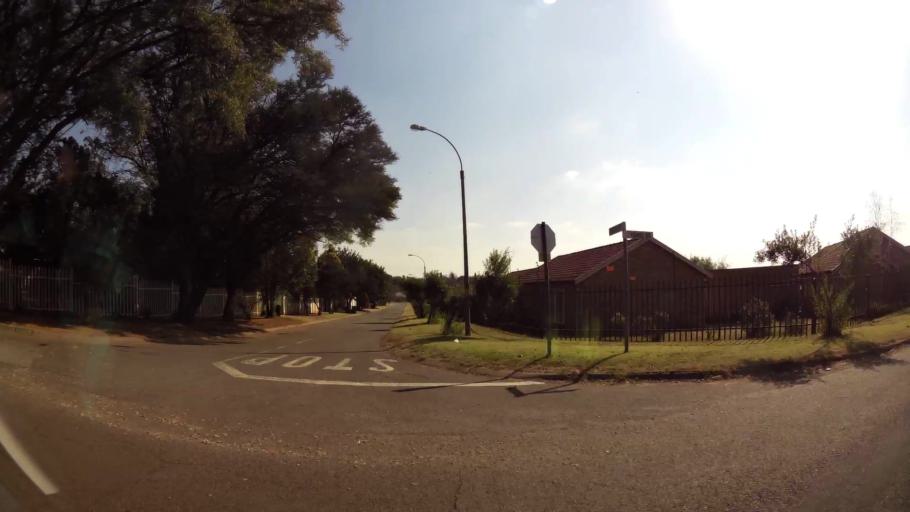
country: ZA
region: Gauteng
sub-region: City of Johannesburg Metropolitan Municipality
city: Modderfontein
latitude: -26.1238
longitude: 28.2245
